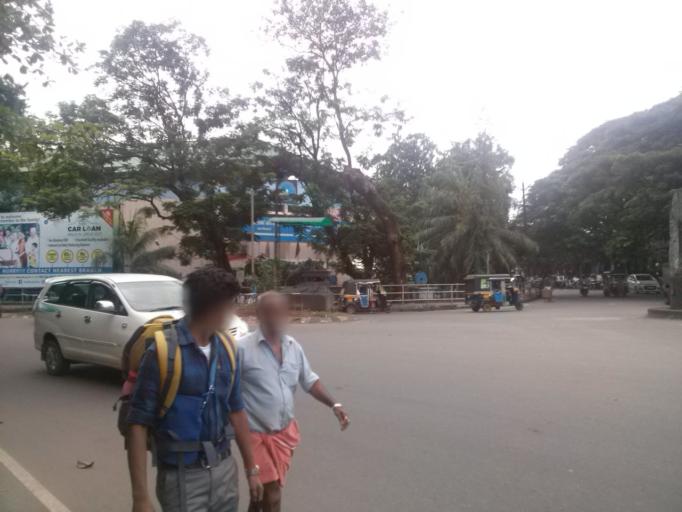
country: IN
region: Kerala
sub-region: Kozhikode
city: Kozhikode
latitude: 11.2555
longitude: 75.7806
